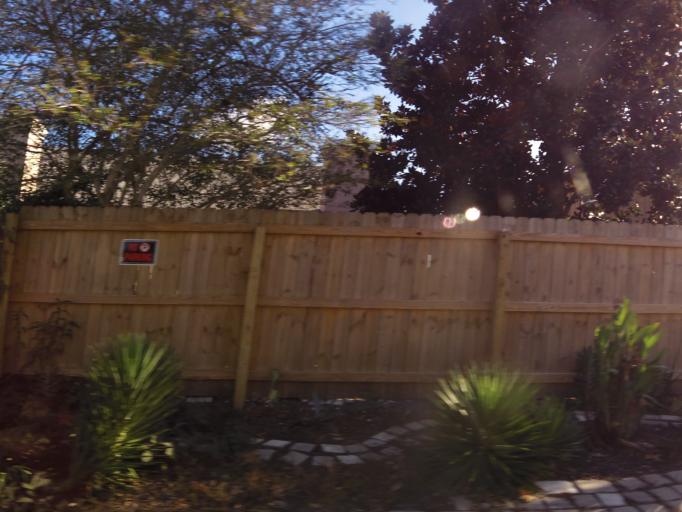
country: US
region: Florida
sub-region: Duval County
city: Jacksonville Beach
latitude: 30.2788
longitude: -81.3939
